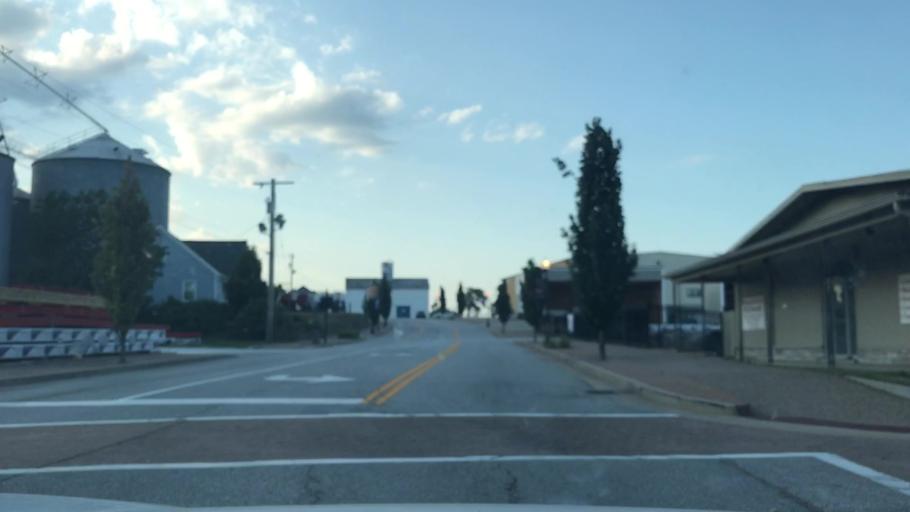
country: US
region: Missouri
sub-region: Saint Charles County
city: Wentzville
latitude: 38.8093
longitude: -90.8539
